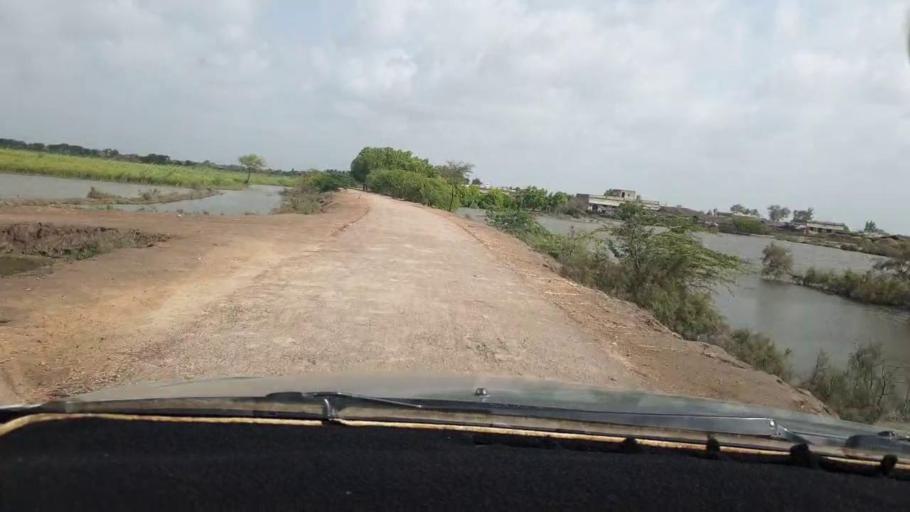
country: PK
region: Sindh
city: Tando Bago
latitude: 24.7881
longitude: 69.0284
